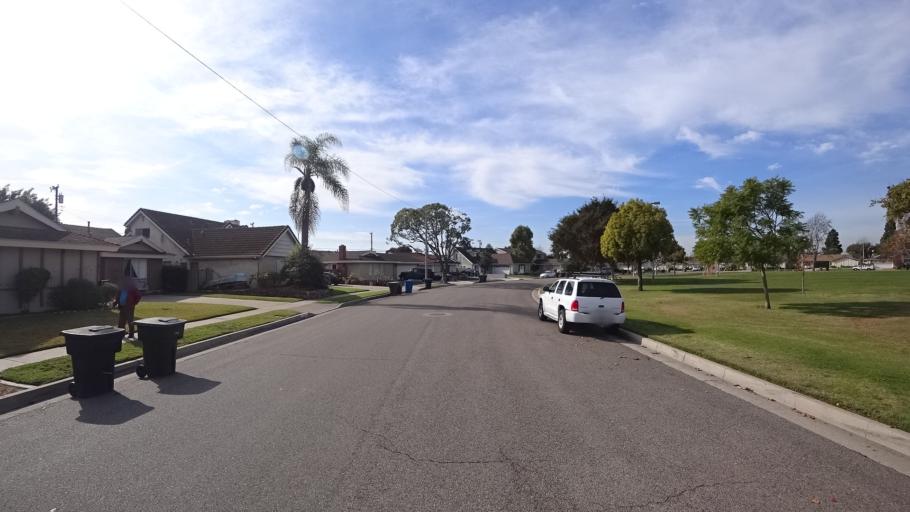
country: US
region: California
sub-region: Orange County
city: Westminster
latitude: 33.7795
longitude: -118.0382
